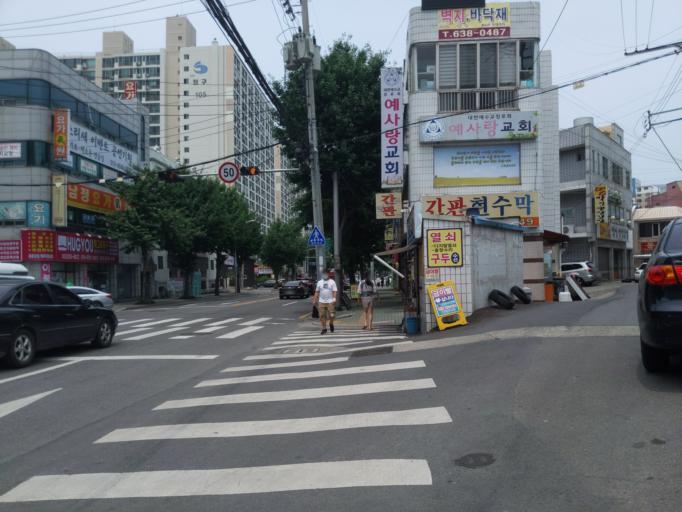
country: KR
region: Daegu
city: Hwawon
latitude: 35.8115
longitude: 128.5256
